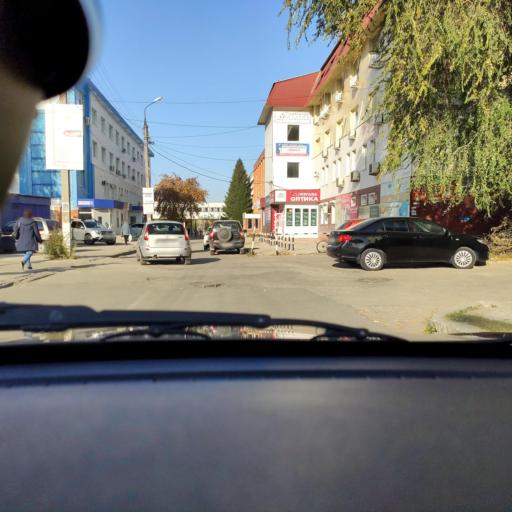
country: RU
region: Samara
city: Tol'yatti
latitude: 53.5224
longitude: 49.4205
